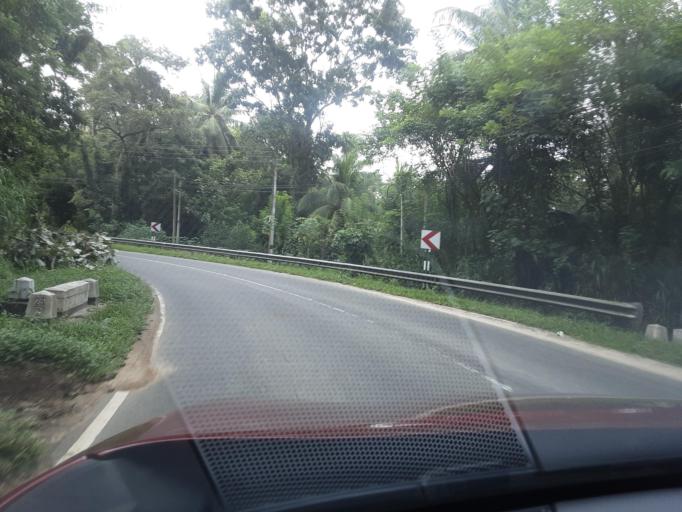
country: LK
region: Uva
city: Monaragala
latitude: 6.8979
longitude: 81.2882
